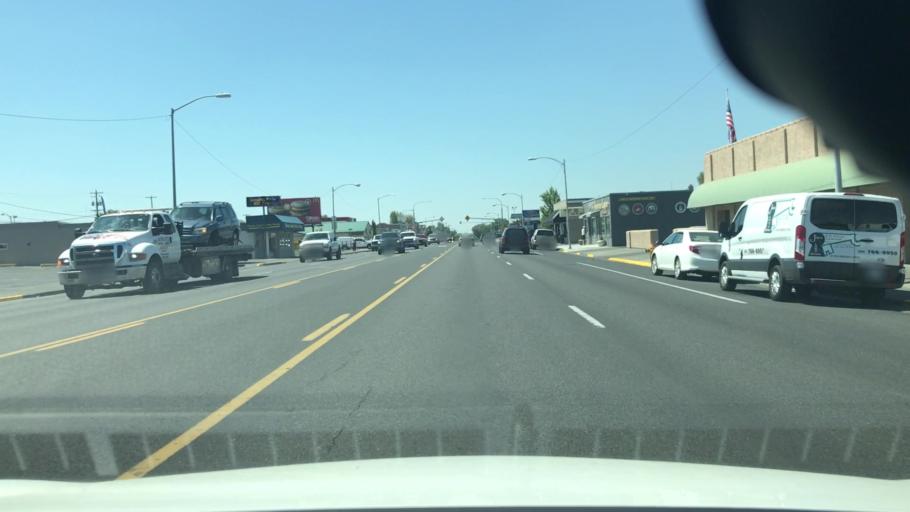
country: US
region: Washington
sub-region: Grant County
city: Moses Lake
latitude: 47.1281
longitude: -119.2848
